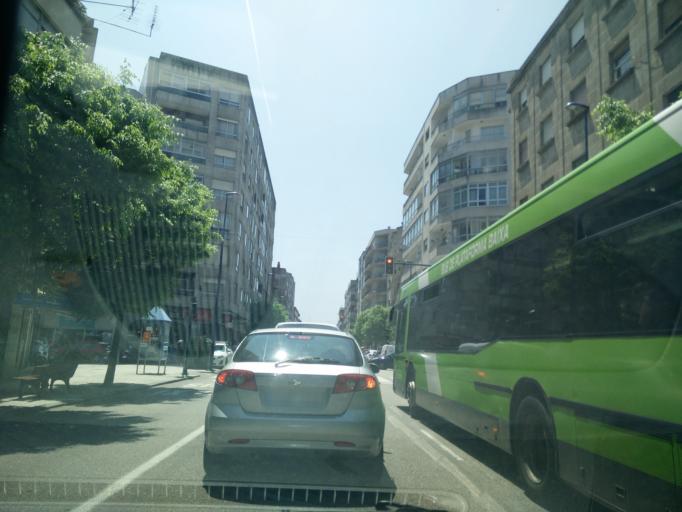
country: ES
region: Galicia
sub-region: Provincia de Pontevedra
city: Vigo
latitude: 42.2199
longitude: -8.7332
